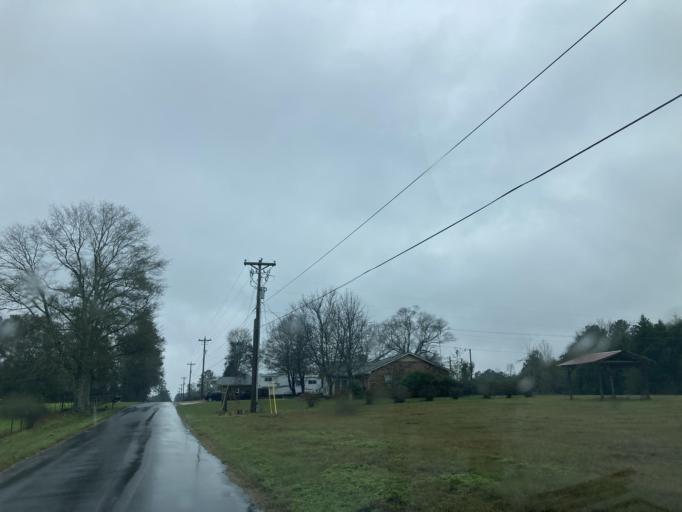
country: US
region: Mississippi
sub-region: Forrest County
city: Rawls Springs
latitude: 31.4864
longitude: -89.3824
